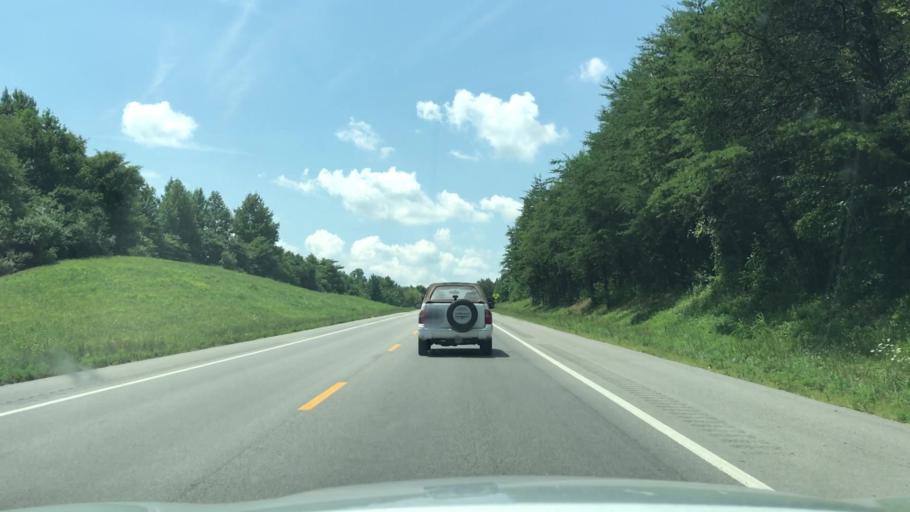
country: US
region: Tennessee
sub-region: Pickett County
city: Byrdstown
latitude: 36.5976
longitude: -85.1223
